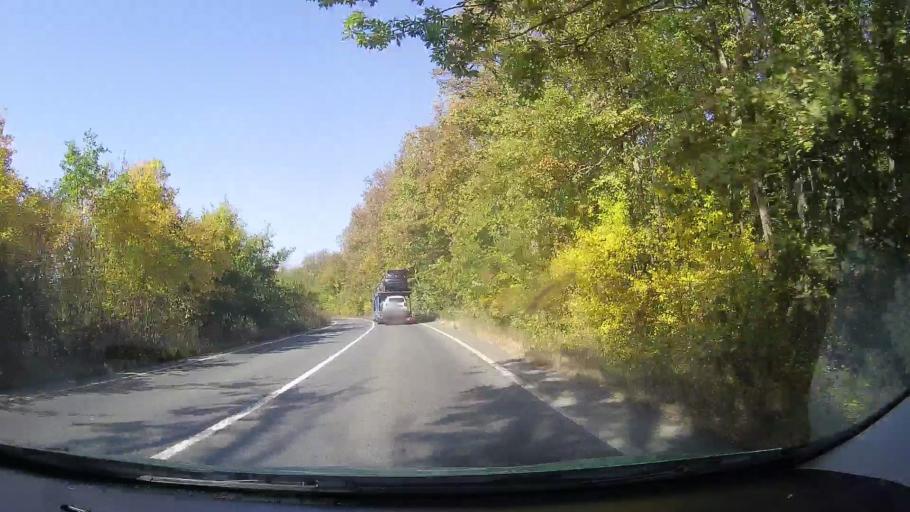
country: RO
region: Arad
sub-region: Comuna Conop
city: Conop
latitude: 46.1121
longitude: 21.8475
